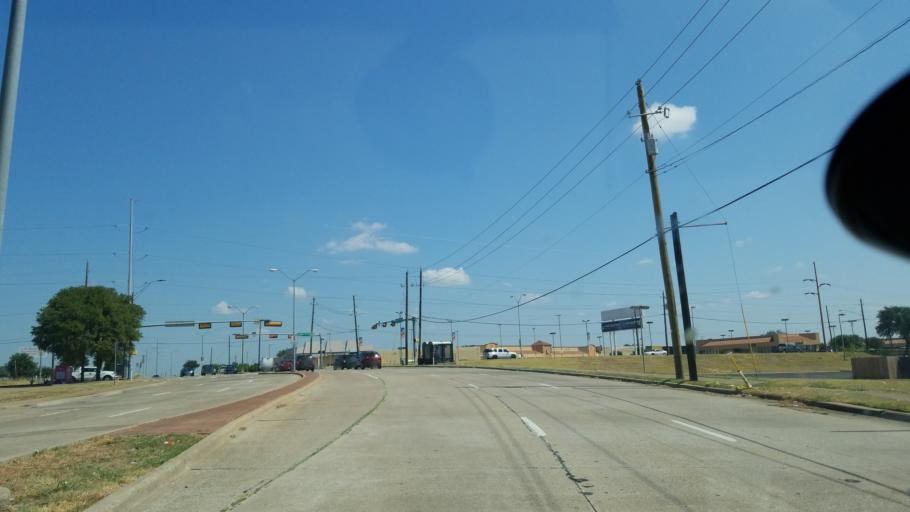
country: US
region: Texas
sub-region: Dallas County
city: Duncanville
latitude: 32.6611
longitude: -96.8818
